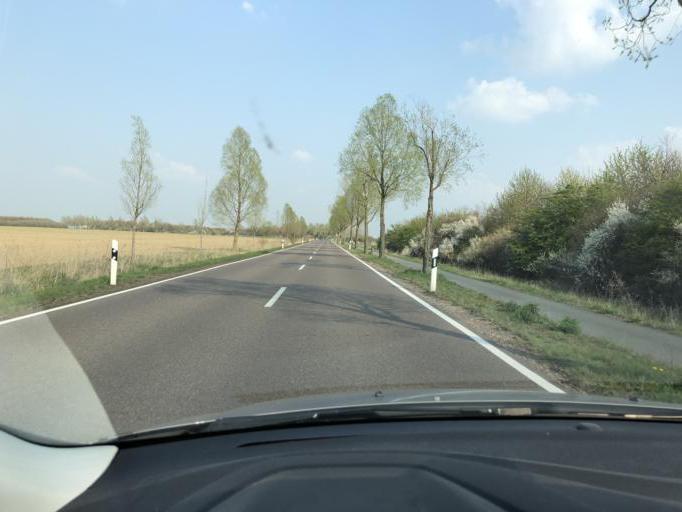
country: DE
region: Saxony
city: Zwochau
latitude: 51.4366
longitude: 12.2639
